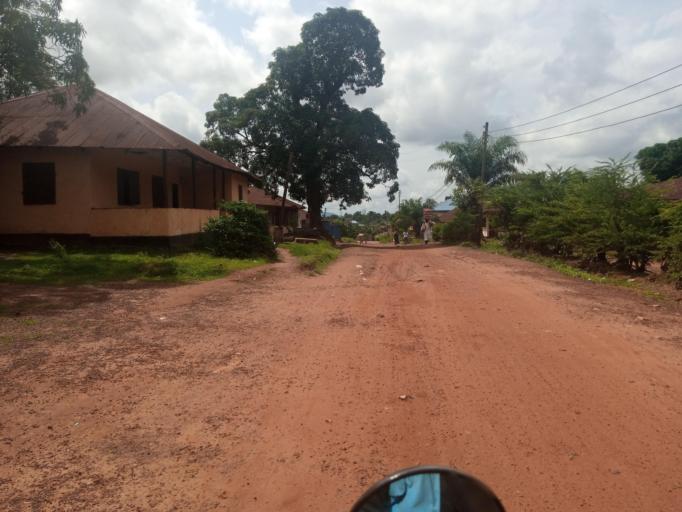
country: SL
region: Southern Province
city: Bo
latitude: 7.9713
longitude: -11.7412
